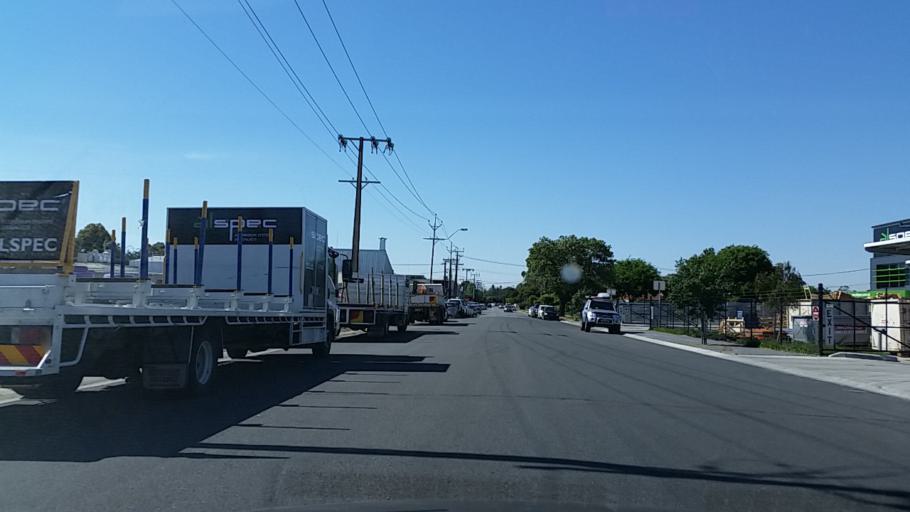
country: AU
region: South Australia
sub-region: Charles Sturt
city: Woodville
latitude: -34.8923
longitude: 138.5450
